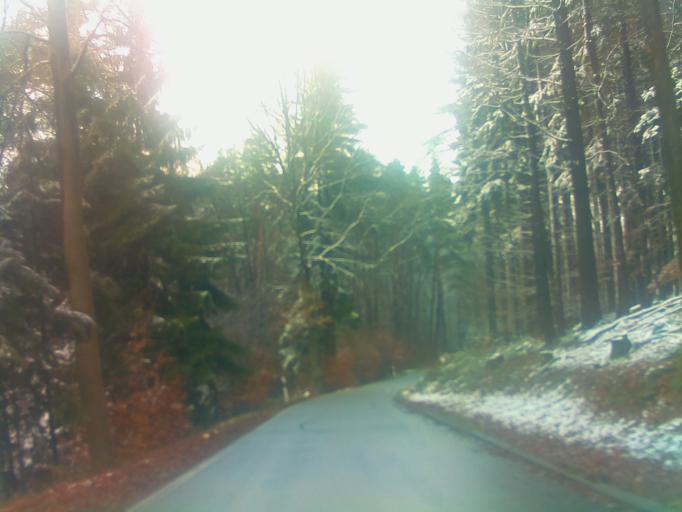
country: DE
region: Hesse
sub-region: Regierungsbezirk Darmstadt
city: Wald-Michelbach
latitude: 49.5553
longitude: 8.8812
